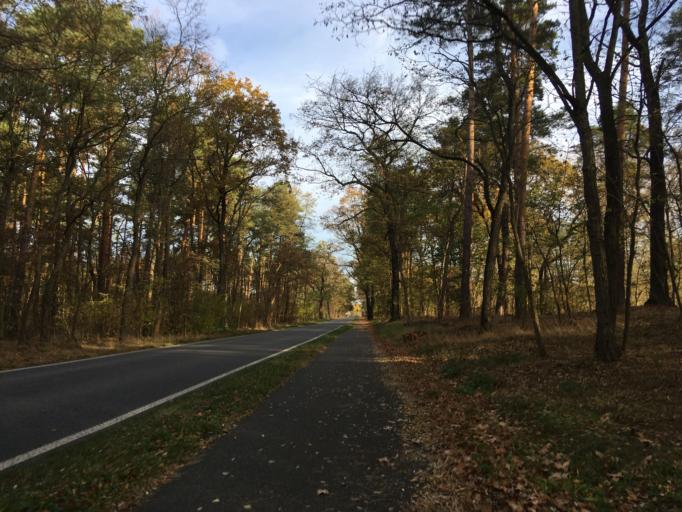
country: DE
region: Brandenburg
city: Luebben
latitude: 51.9605
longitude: 13.8837
